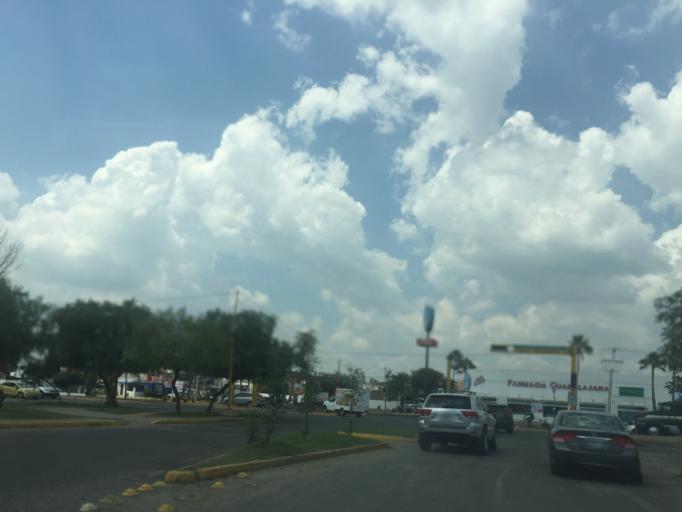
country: MX
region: Guanajuato
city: Leon
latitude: 21.1706
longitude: -101.6795
